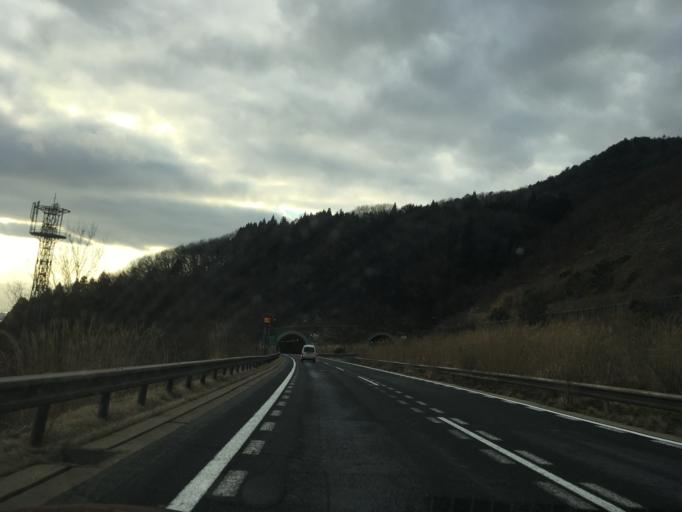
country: JP
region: Yamagata
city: Yamagata-shi
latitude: 38.2434
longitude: 140.4027
